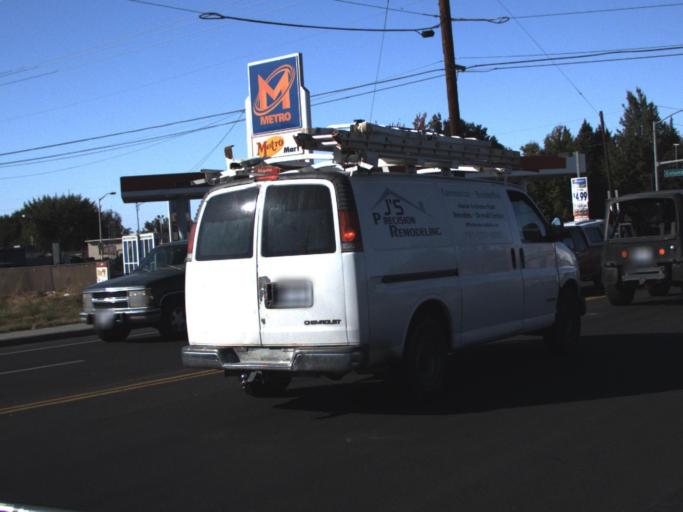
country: US
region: Washington
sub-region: Franklin County
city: Pasco
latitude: 46.2113
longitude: -119.1071
